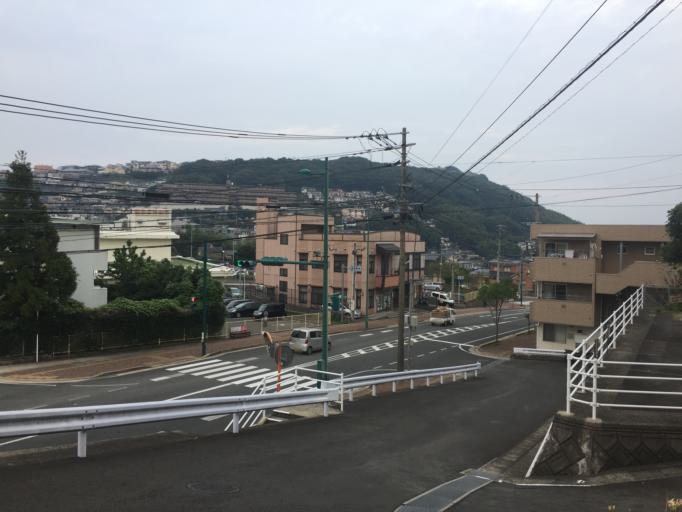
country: JP
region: Nagasaki
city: Nagasaki-shi
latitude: 32.7280
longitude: 129.8892
